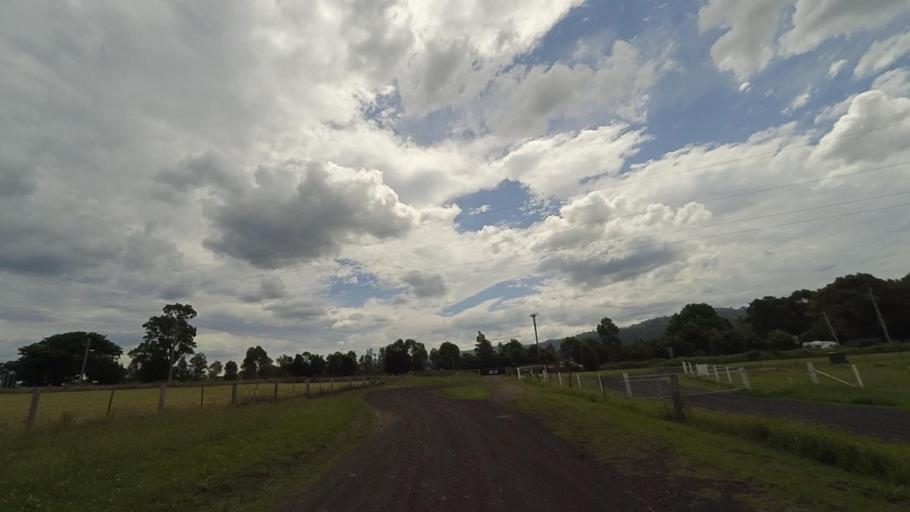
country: AU
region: New South Wales
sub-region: Shoalhaven Shire
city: Berry
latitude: -34.7918
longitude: 150.6726
